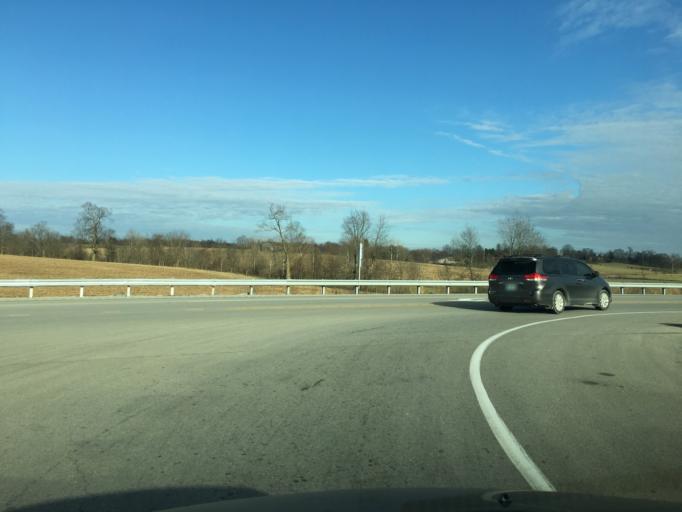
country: US
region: Kentucky
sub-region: Scott County
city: Georgetown
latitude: 38.2427
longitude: -84.5829
